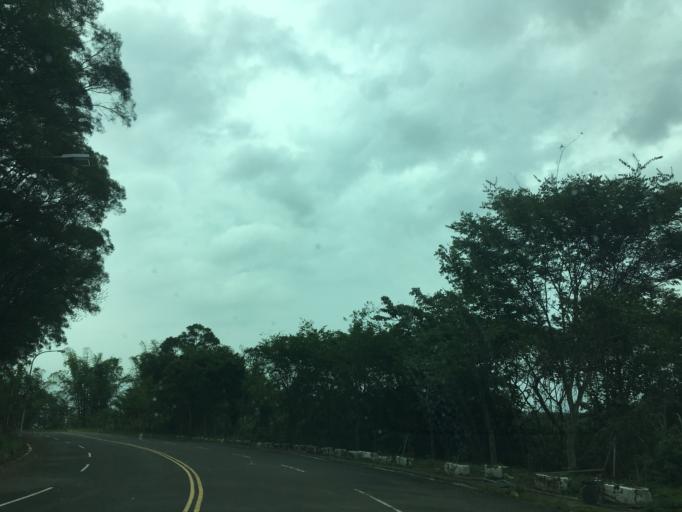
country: TW
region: Taiwan
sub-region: Taichung City
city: Taichung
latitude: 24.0624
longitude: 120.7253
